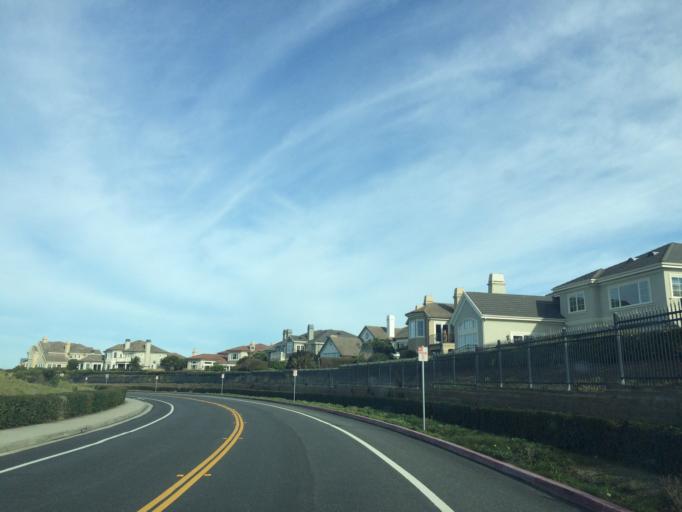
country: US
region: California
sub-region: San Mateo County
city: Half Moon Bay
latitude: 37.4316
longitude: -122.4376
